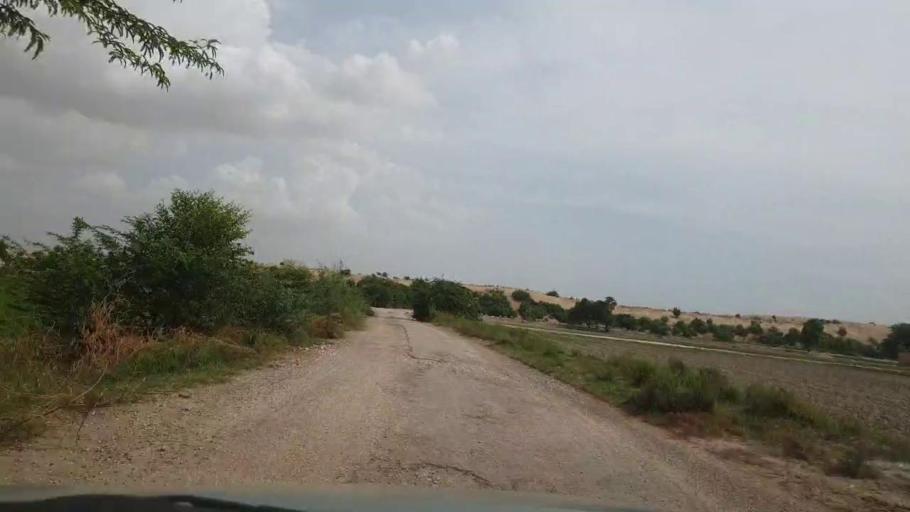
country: PK
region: Sindh
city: Bozdar
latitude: 27.0783
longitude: 69.0135
